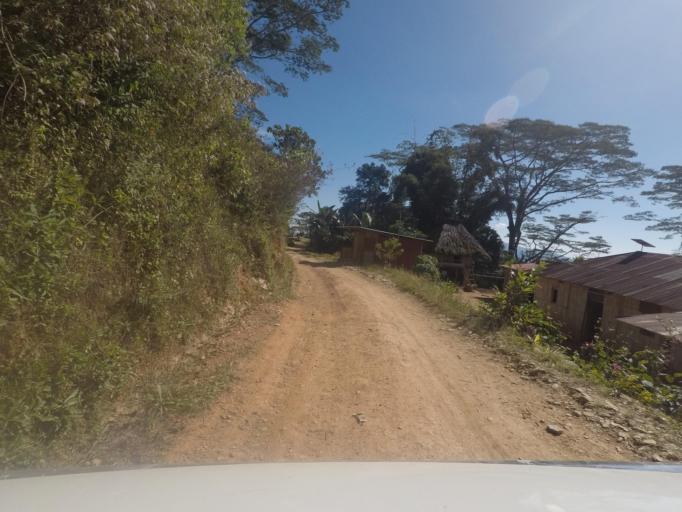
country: TL
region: Ermera
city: Gleno
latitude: -8.7345
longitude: 125.3435
